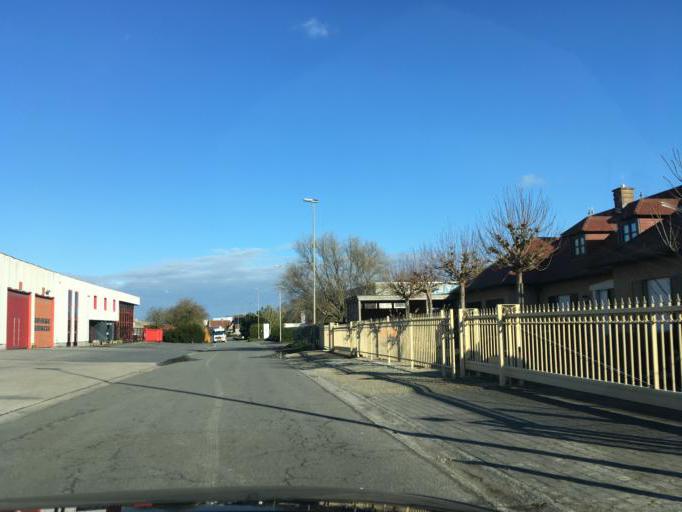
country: BE
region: Flanders
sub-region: Provincie West-Vlaanderen
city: Roeselare
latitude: 50.9267
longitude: 3.1159
